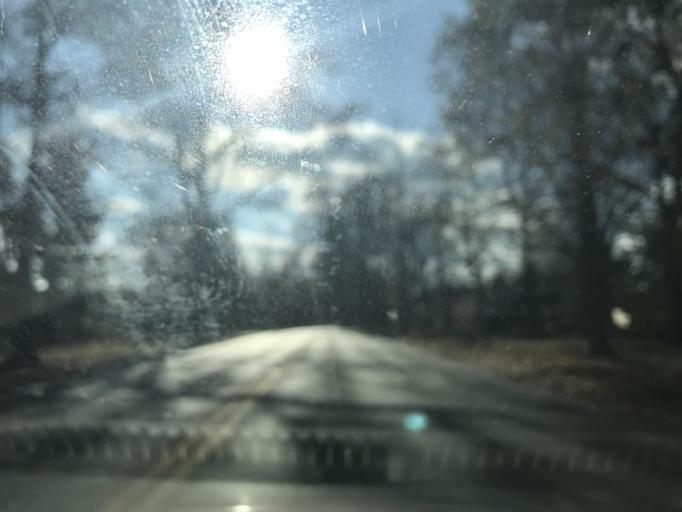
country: US
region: Kentucky
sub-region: Jefferson County
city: Audubon Park
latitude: 38.2214
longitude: -85.7326
